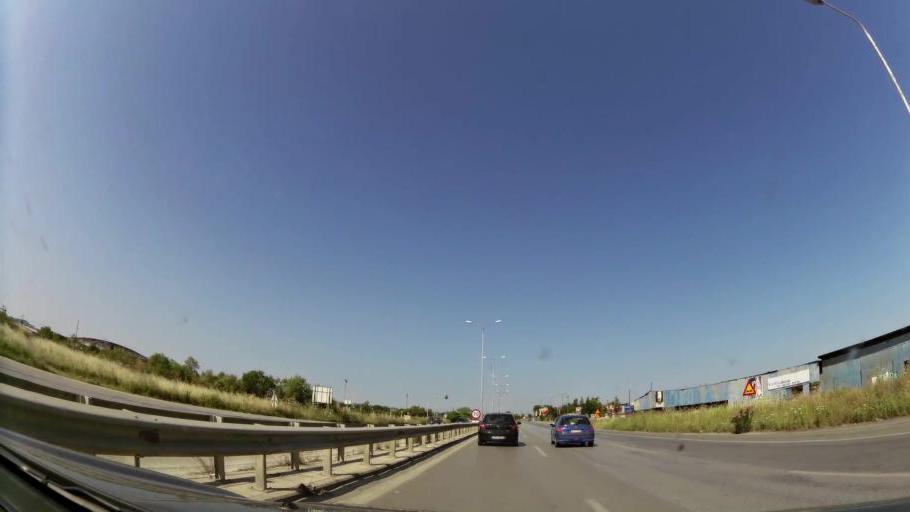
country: GR
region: Central Macedonia
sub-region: Nomos Thessalonikis
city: Neo Rysi
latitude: 40.5126
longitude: 22.9862
